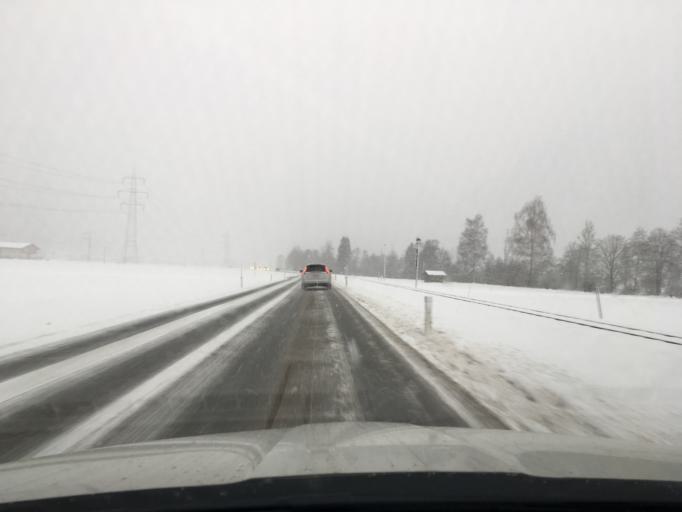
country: AT
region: Tyrol
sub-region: Politischer Bezirk Schwaz
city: Schwendau
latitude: 47.1868
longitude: 11.8664
